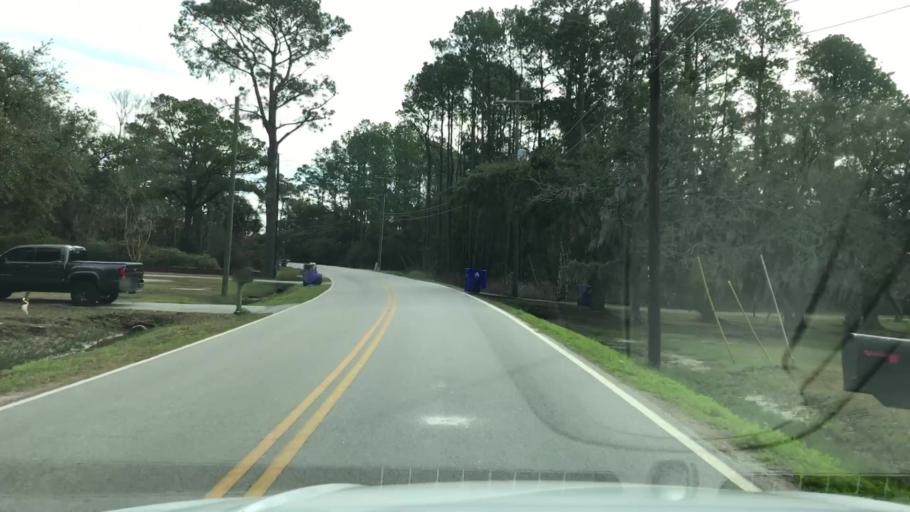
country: US
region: South Carolina
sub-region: Charleston County
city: Charleston
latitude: 32.7754
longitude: -80.0177
